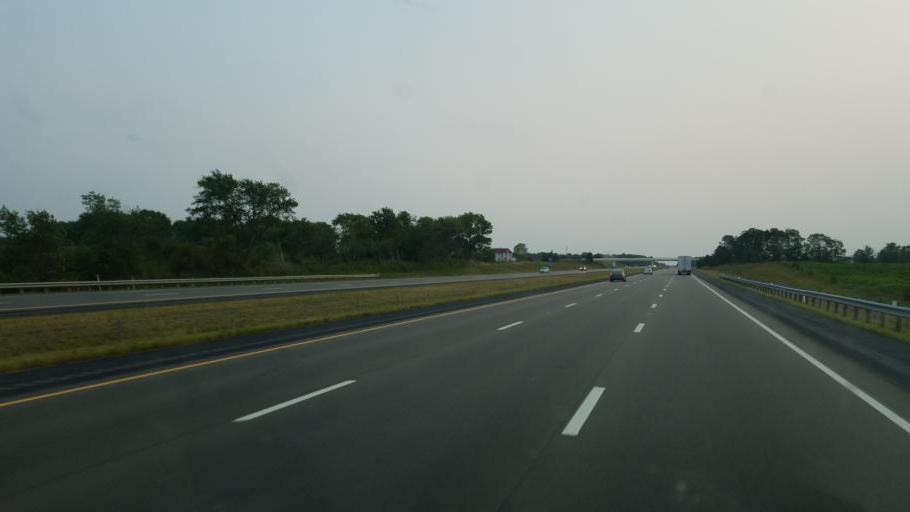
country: US
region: Ohio
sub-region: Medina County
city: Medina
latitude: 41.0822
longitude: -81.8365
